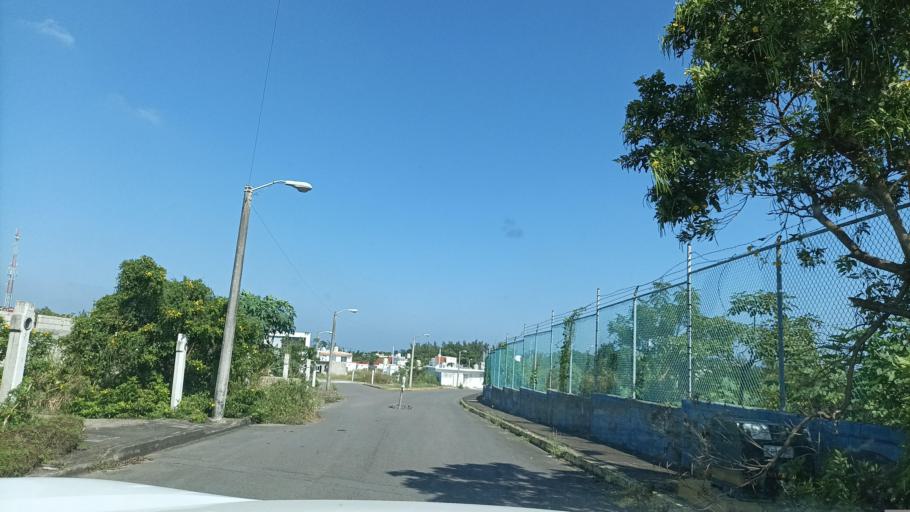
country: MX
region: Veracruz
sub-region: Veracruz
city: Rio Medio [Granja]
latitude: 19.2013
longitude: -96.1797
